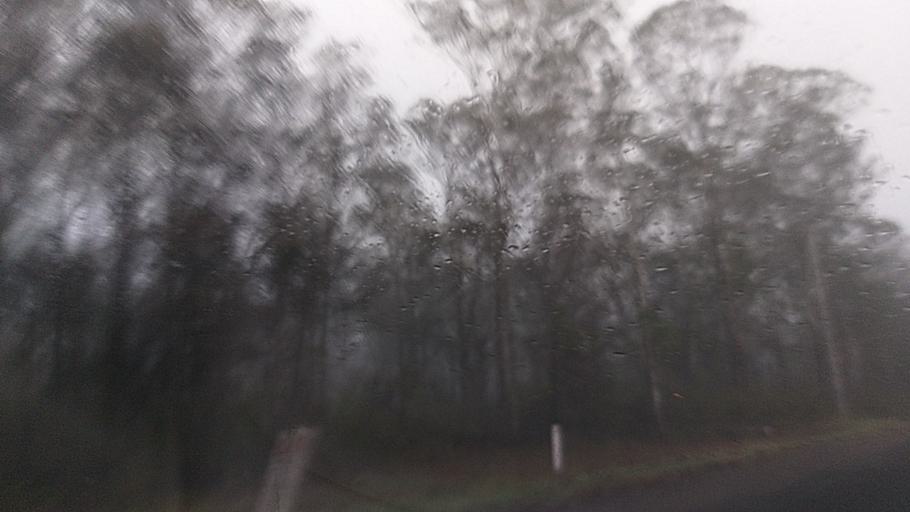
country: AU
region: New South Wales
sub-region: Wollondilly
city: Douglas Park
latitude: -34.2007
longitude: 150.7090
